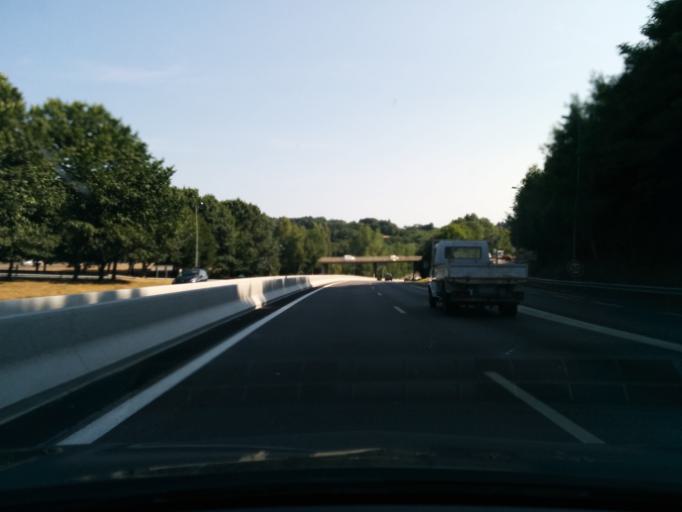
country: FR
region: Limousin
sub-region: Departement de la Haute-Vienne
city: Condat-sur-Vienne
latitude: 45.8088
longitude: 1.2978
